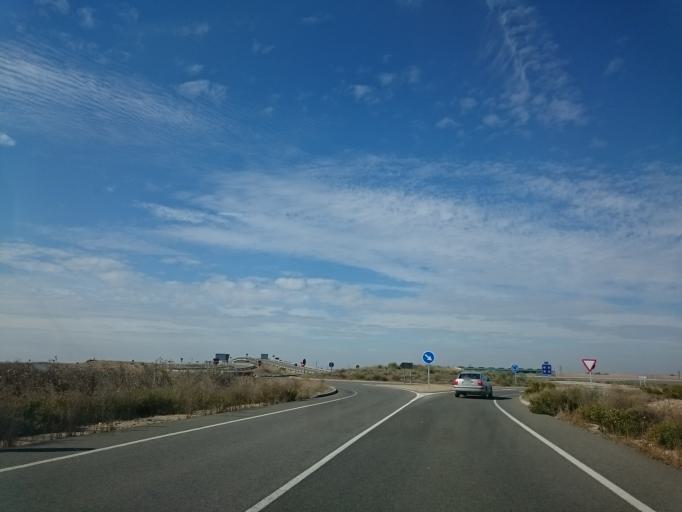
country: ES
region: Catalonia
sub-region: Provincia de Lleida
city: Alguaire
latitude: 41.7334
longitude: 0.5636
